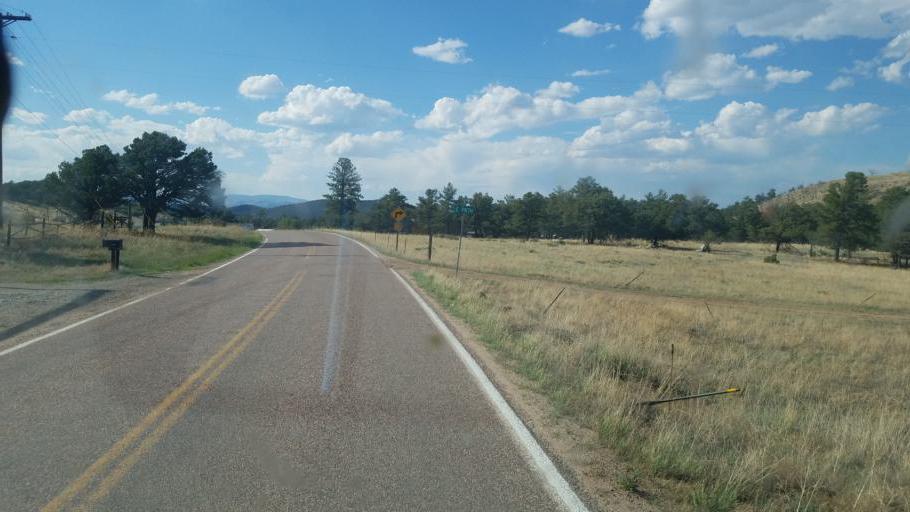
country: US
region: Colorado
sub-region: Custer County
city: Westcliffe
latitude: 38.3348
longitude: -105.4850
